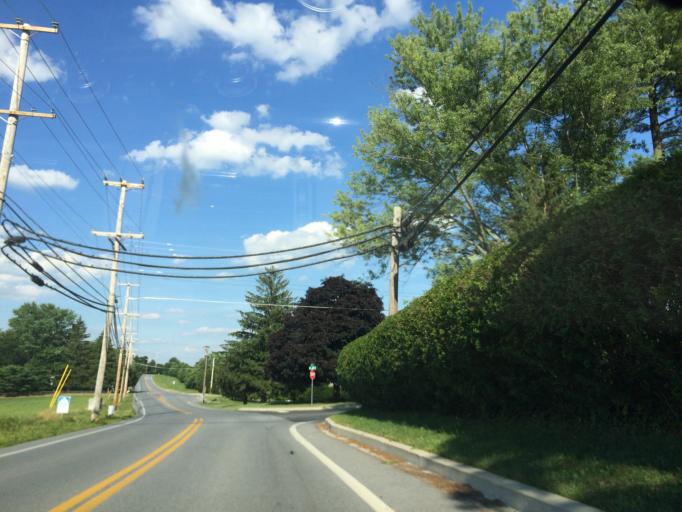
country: US
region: Maryland
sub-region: Carroll County
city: Sykesville
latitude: 39.3794
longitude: -76.9869
